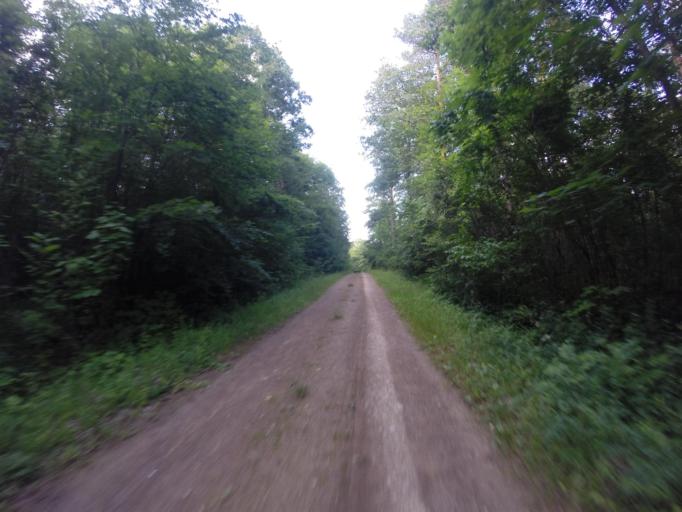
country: DE
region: Thuringia
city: Golmsdorf
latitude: 50.9483
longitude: 11.6713
